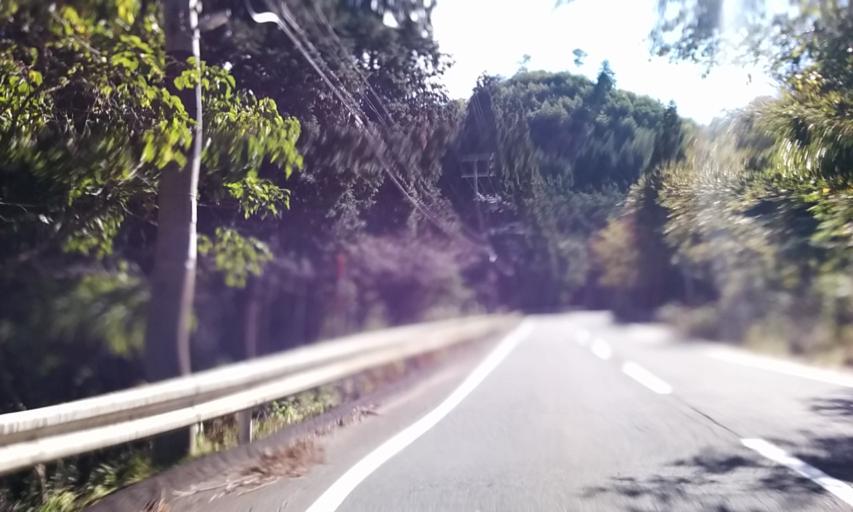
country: JP
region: Kyoto
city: Kameoka
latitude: 35.1988
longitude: 135.6202
